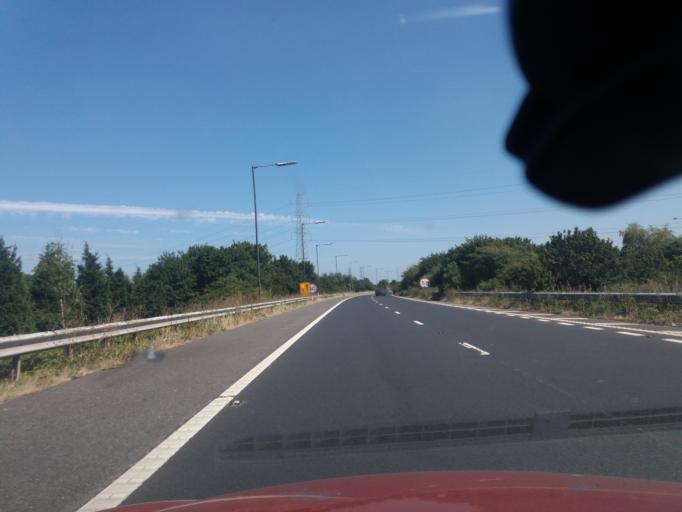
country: GB
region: England
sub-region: Borough of Bolton
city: Kearsley
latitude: 53.5303
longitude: -2.3718
